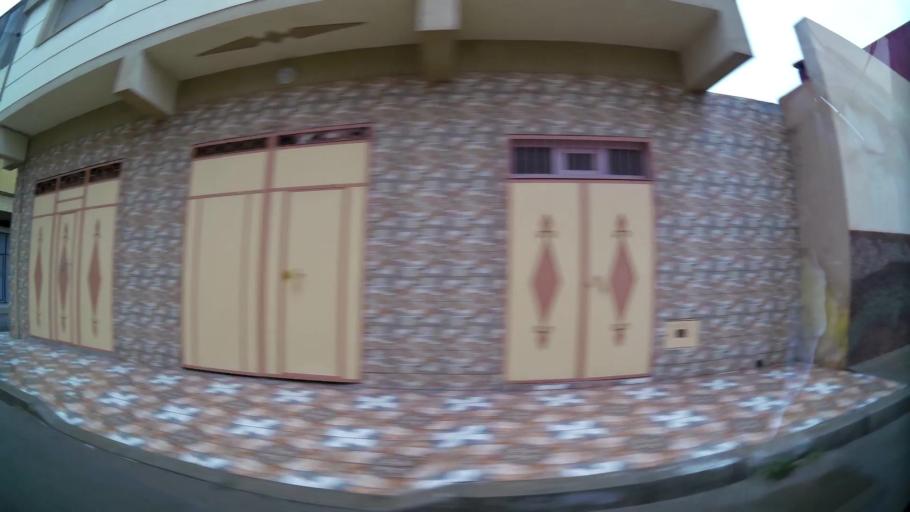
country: MA
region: Oriental
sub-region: Nador
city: Nador
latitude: 35.1643
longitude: -2.9539
